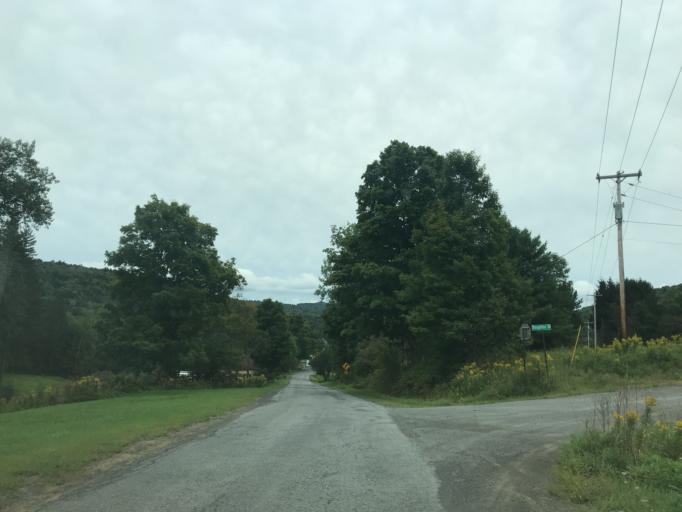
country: US
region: New York
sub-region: Otsego County
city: Worcester
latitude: 42.5670
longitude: -74.6706
